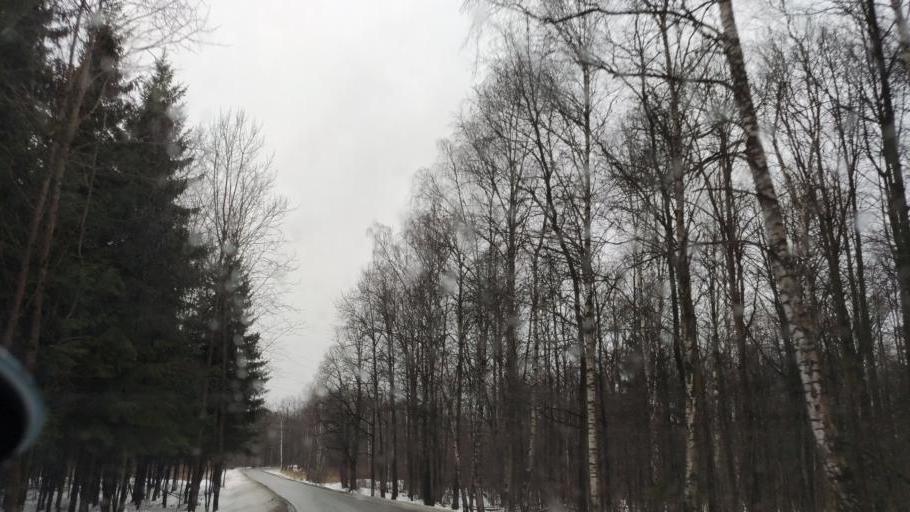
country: RU
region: Moskovskaya
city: Vatutinki
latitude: 55.4773
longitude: 37.3400
